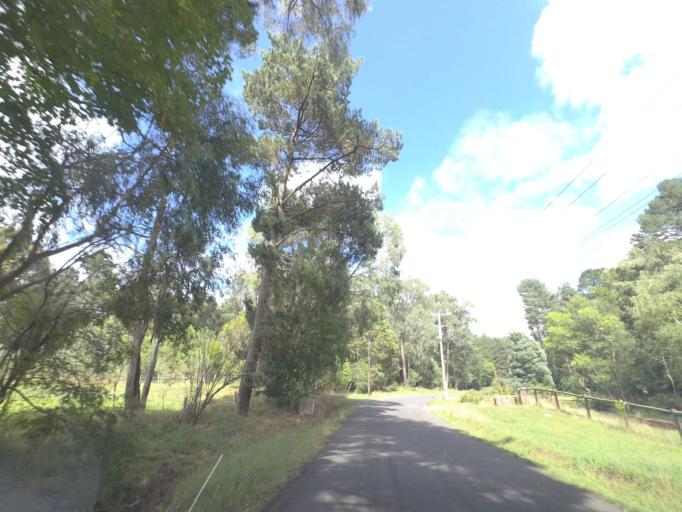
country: AU
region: Victoria
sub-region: Yarra Ranges
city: Mount Evelyn
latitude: -37.7948
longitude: 145.3996
